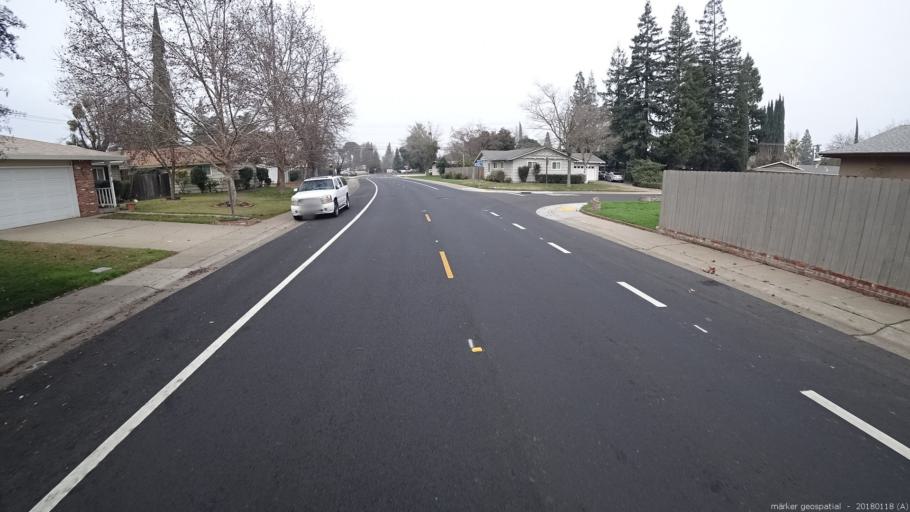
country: US
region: California
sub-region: Sacramento County
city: Rancho Cordova
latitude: 38.5884
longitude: -121.3152
